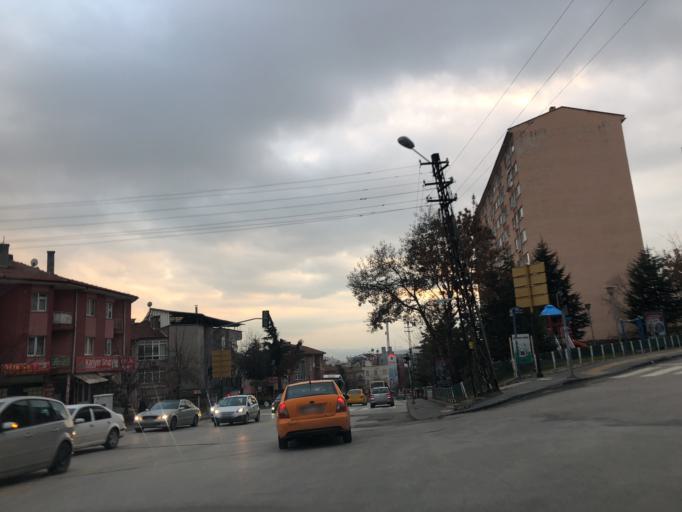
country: TR
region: Ankara
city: Ankara
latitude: 39.9722
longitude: 32.8107
